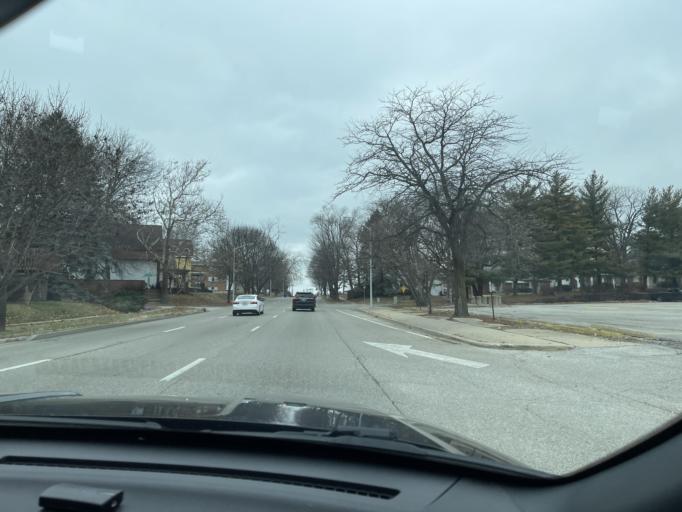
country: US
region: Illinois
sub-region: Sangamon County
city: Springfield
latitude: 39.8036
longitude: -89.6643
